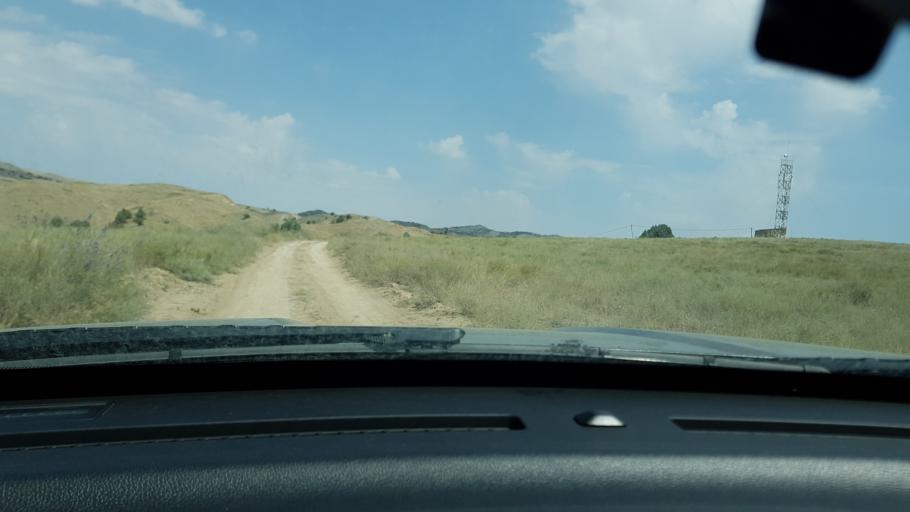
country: TM
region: Ahal
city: Baharly
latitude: 38.4114
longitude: 56.9241
